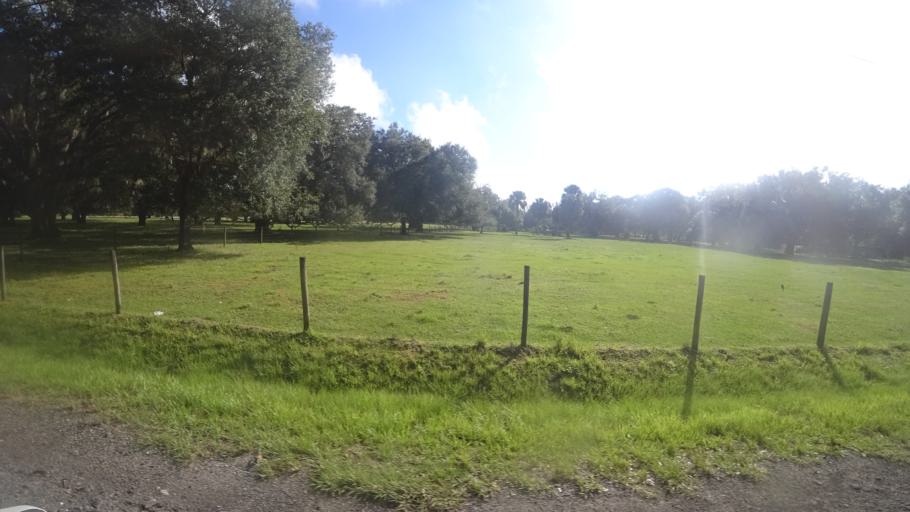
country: US
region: Florida
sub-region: Manatee County
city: Ellenton
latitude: 27.5730
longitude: -82.3924
